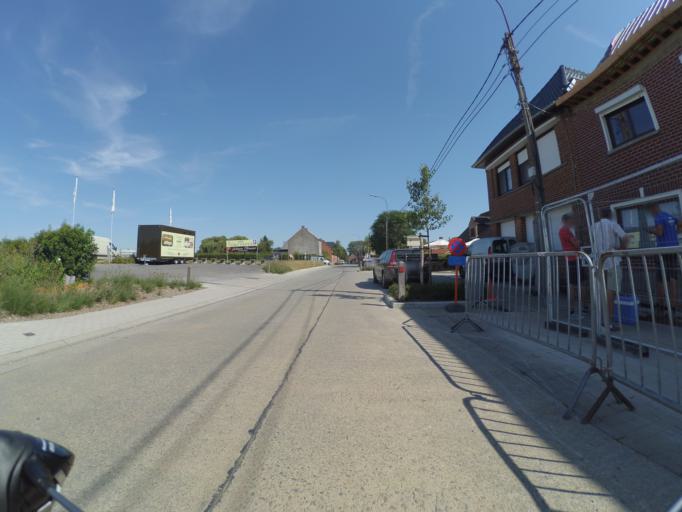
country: BE
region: Flanders
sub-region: Provincie Oost-Vlaanderen
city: Oudenaarde
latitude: 50.8065
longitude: 3.6225
